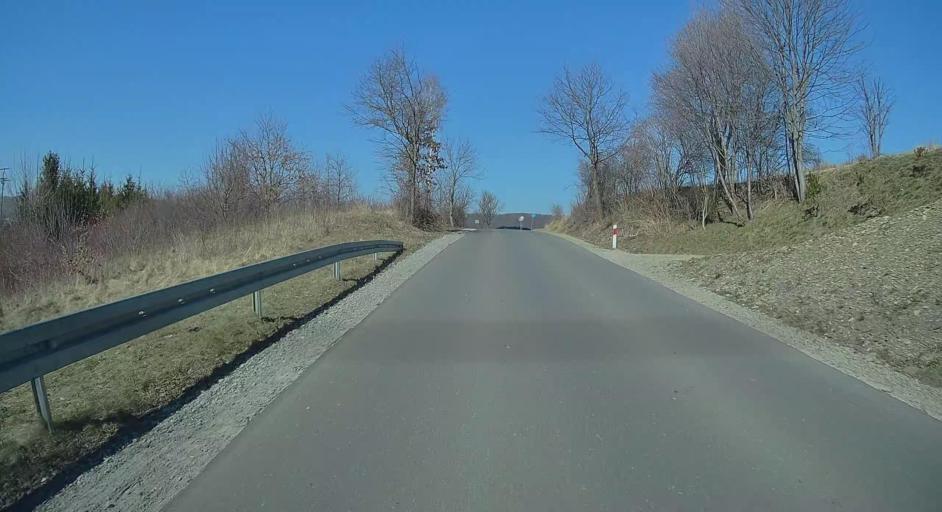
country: PL
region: Subcarpathian Voivodeship
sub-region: Powiat brzozowski
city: Nozdrzec
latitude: 49.7726
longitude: 22.2231
